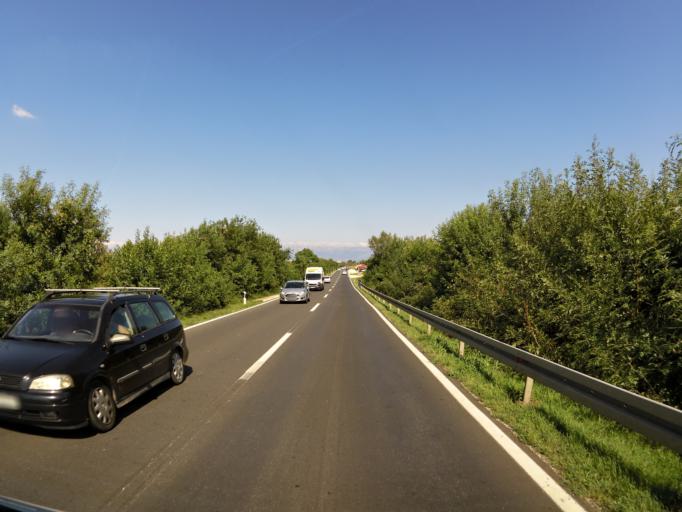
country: HR
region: Zadarska
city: Policnik
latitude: 44.1530
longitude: 15.3350
